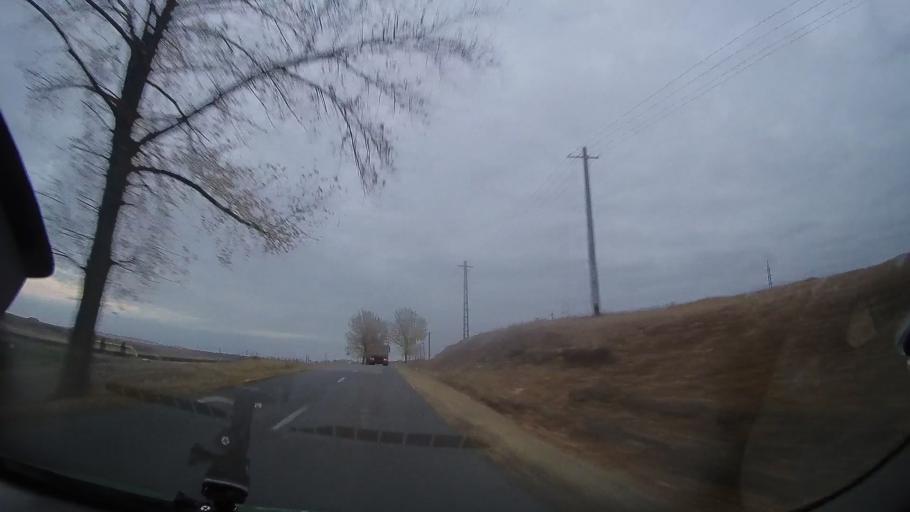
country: RO
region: Tulcea
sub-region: Comuna Mihai Bravu
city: Mihai Bravu
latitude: 44.9597
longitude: 28.6451
